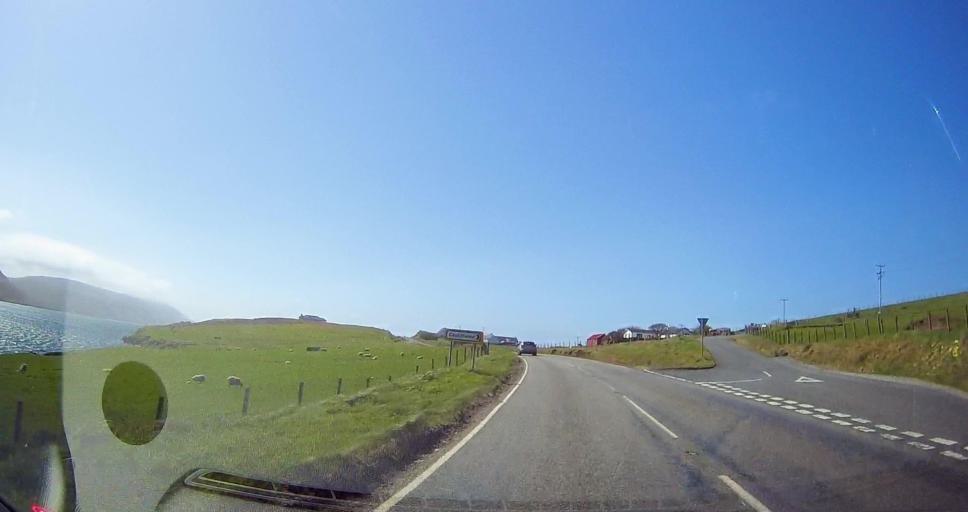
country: GB
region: Scotland
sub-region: Shetland Islands
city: Sandwick
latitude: 60.1259
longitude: -1.2834
